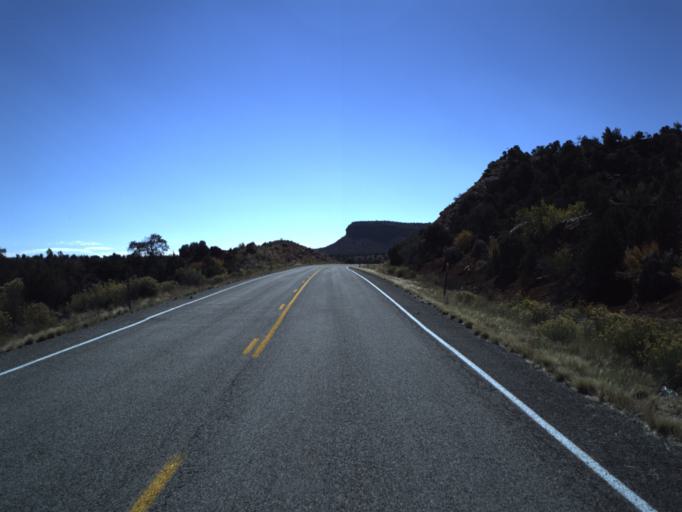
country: US
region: Utah
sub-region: San Juan County
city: Blanding
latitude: 37.5882
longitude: -110.0407
